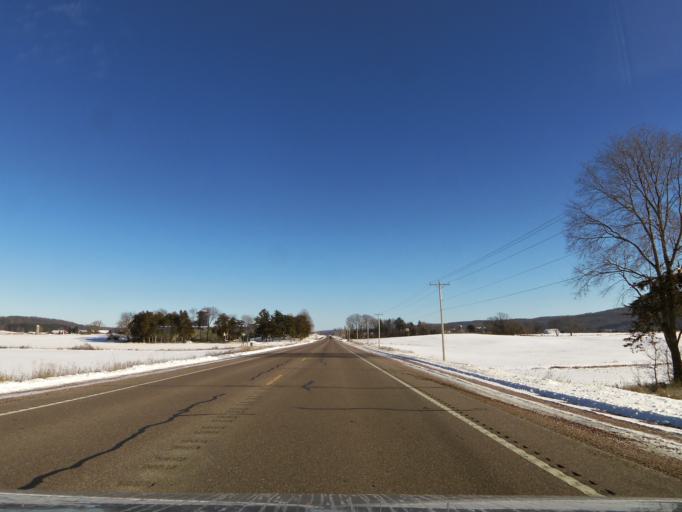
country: US
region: Wisconsin
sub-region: Sauk County
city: Baraboo
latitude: 43.4744
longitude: -89.6877
